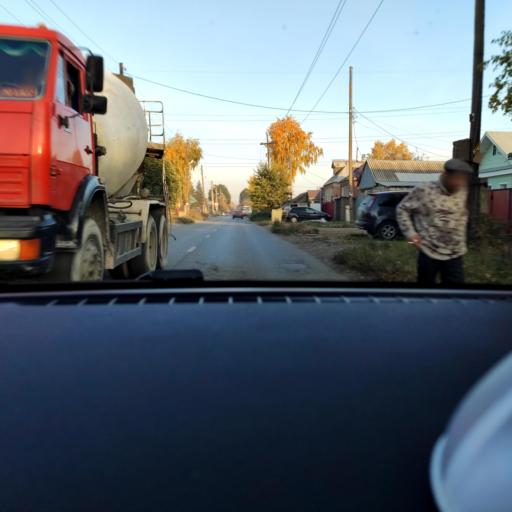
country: RU
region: Samara
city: Petra-Dubrava
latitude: 53.2548
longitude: 50.3166
